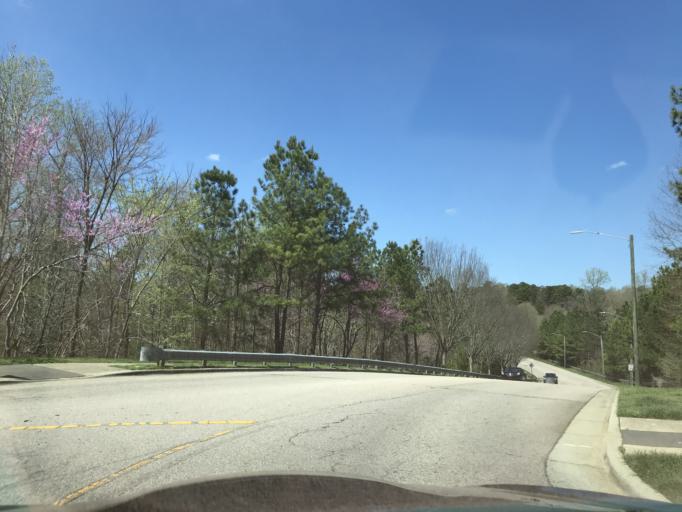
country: US
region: North Carolina
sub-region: Wake County
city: Cary
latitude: 35.8738
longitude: -78.7192
